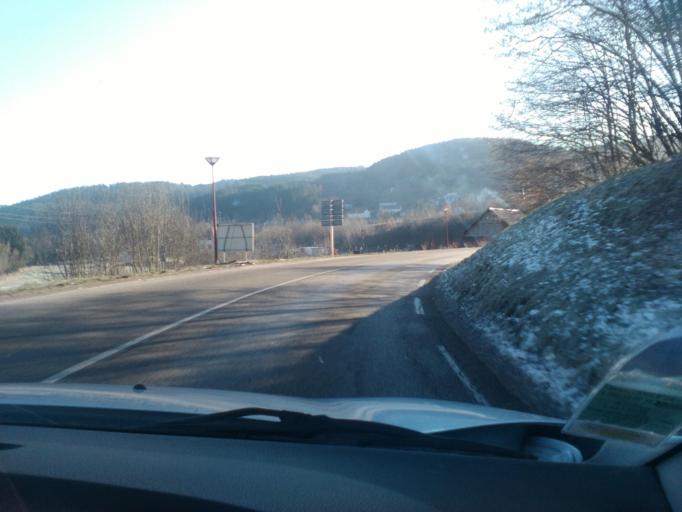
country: FR
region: Alsace
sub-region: Departement du Bas-Rhin
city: Rothau
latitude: 48.4045
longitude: 7.1572
